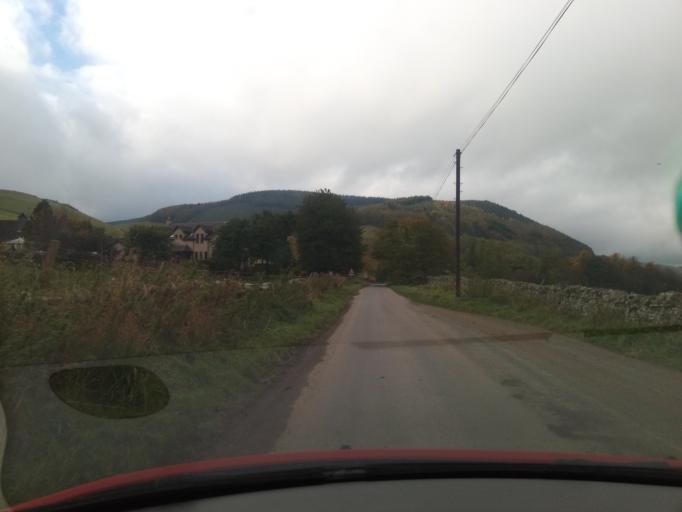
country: GB
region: Scotland
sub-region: The Scottish Borders
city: Innerleithen
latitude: 55.6211
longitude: -3.0055
